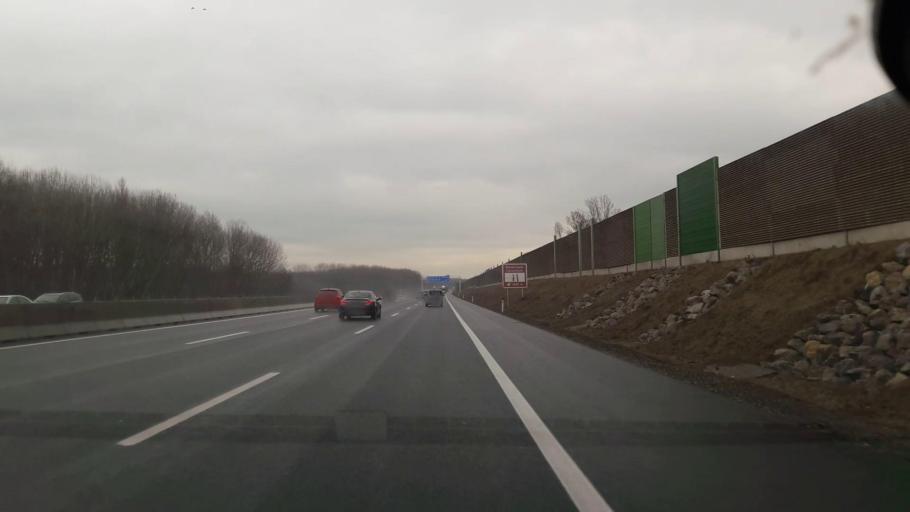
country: AT
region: Lower Austria
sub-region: Politischer Bezirk Wien-Umgebung
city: Fischamend Dorf
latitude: 48.1230
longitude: 16.6090
